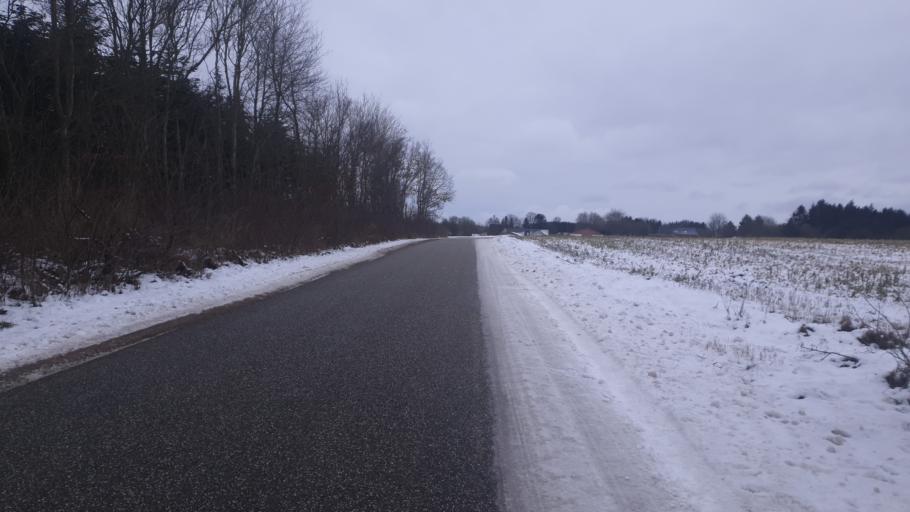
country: DK
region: Central Jutland
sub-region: Hedensted Kommune
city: Hedensted
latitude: 55.7973
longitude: 9.7064
